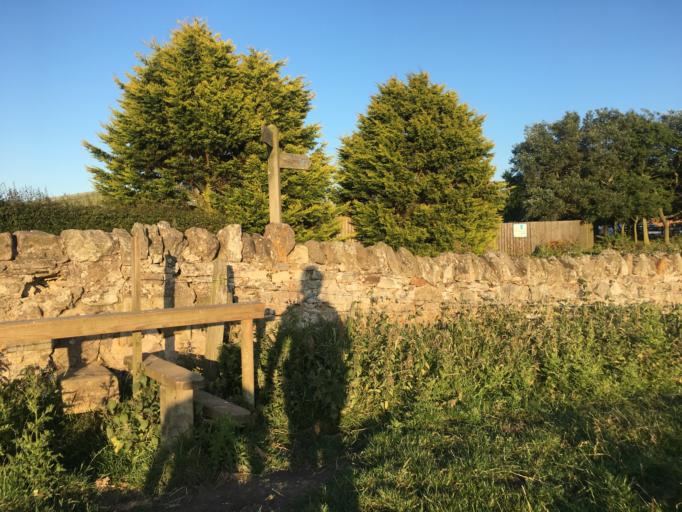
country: GB
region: England
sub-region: Northumberland
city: North Sunderland
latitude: 55.5792
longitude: -1.6683
